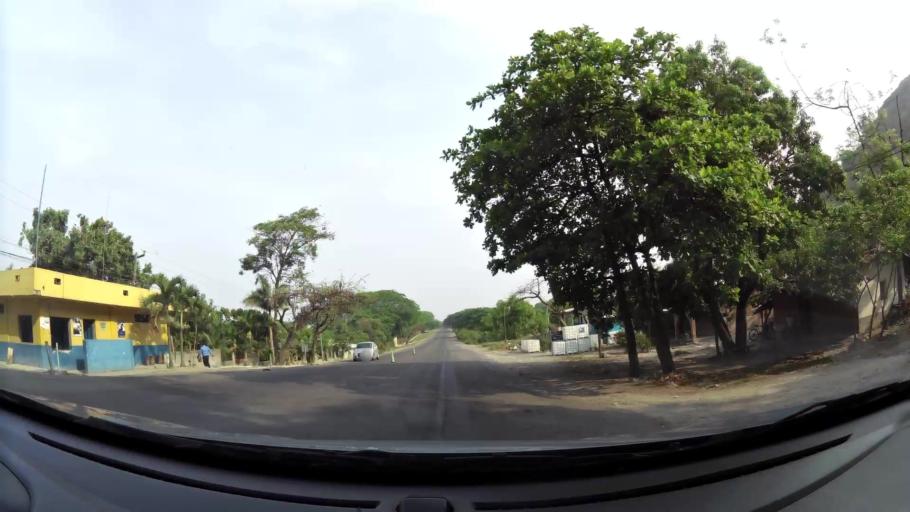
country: HN
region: Comayagua
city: Flores
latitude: 14.2762
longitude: -87.5612
